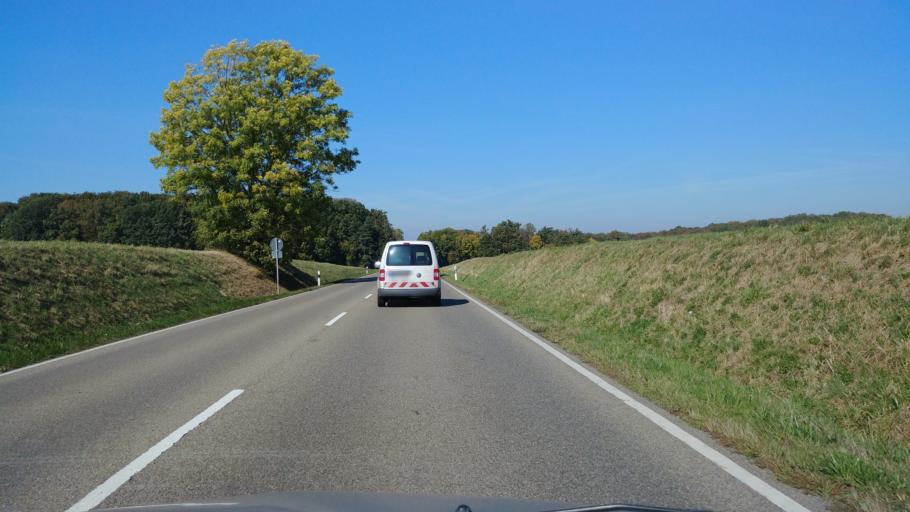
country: DE
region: Baden-Wuerttemberg
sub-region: Regierungsbezirk Stuttgart
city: Untermunkheim
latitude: 49.1811
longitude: 9.7056
